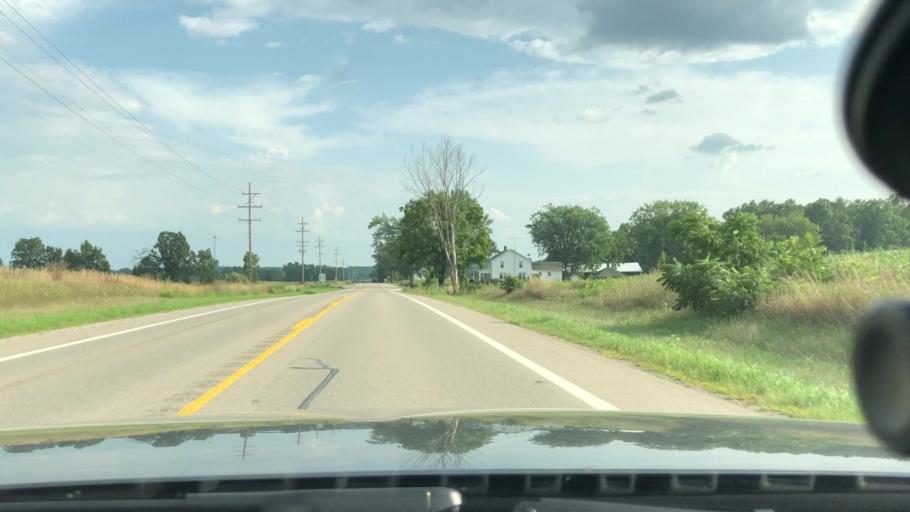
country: US
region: Michigan
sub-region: Washtenaw County
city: Chelsea
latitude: 42.2603
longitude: -84.0340
